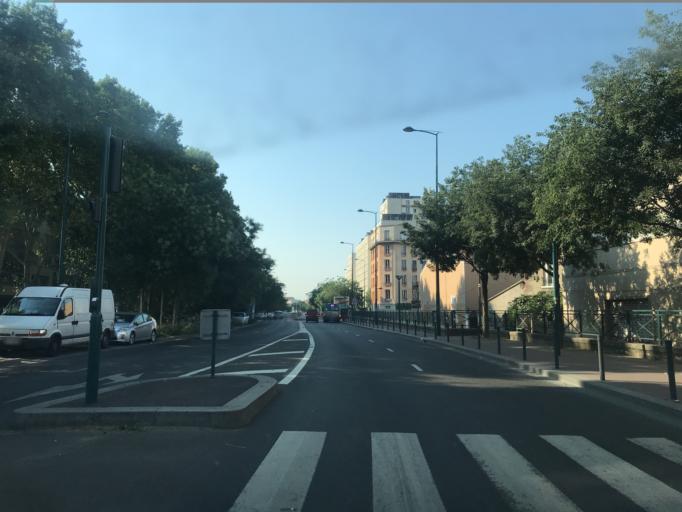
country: FR
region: Ile-de-France
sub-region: Departement des Hauts-de-Seine
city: Asnieres-sur-Seine
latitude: 48.9263
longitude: 2.2846
